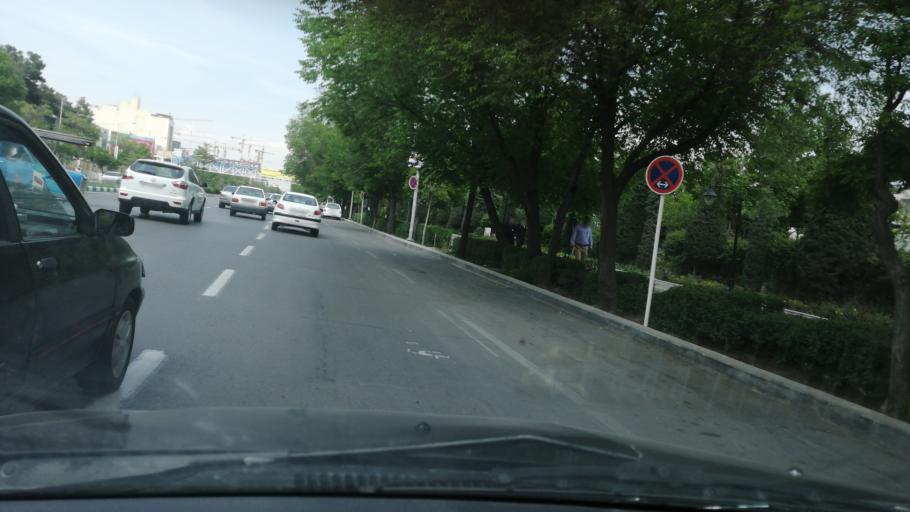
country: IR
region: Razavi Khorasan
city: Mashhad
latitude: 36.3088
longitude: 59.5539
